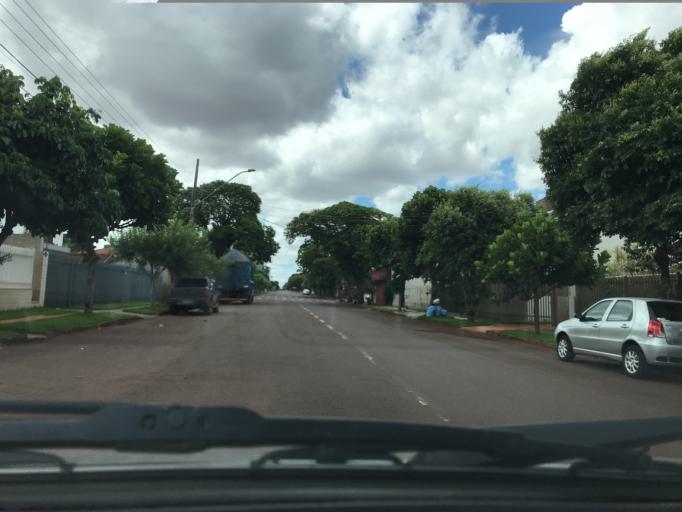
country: BR
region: Parana
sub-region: Palotina
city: Palotina
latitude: -24.2890
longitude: -53.8369
